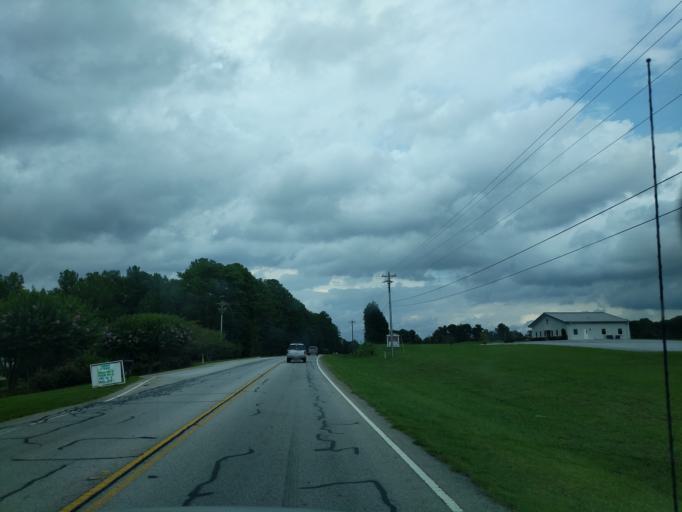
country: US
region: Georgia
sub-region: Walton County
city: Loganville
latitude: 33.8079
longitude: -83.9472
